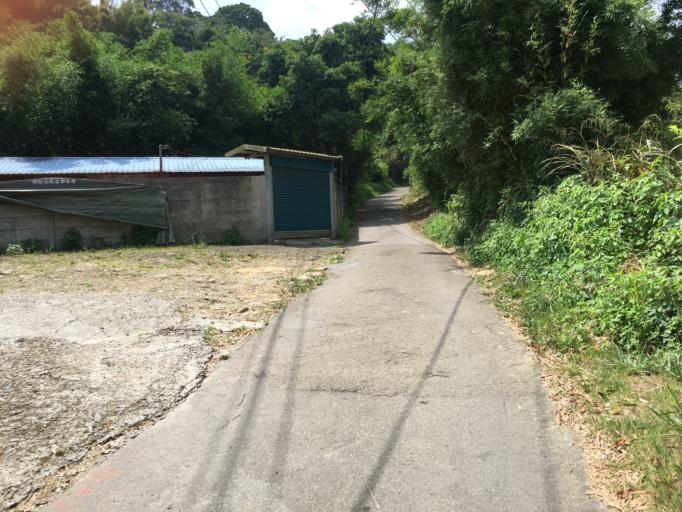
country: TW
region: Taiwan
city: Daxi
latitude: 24.8245
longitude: 121.2308
